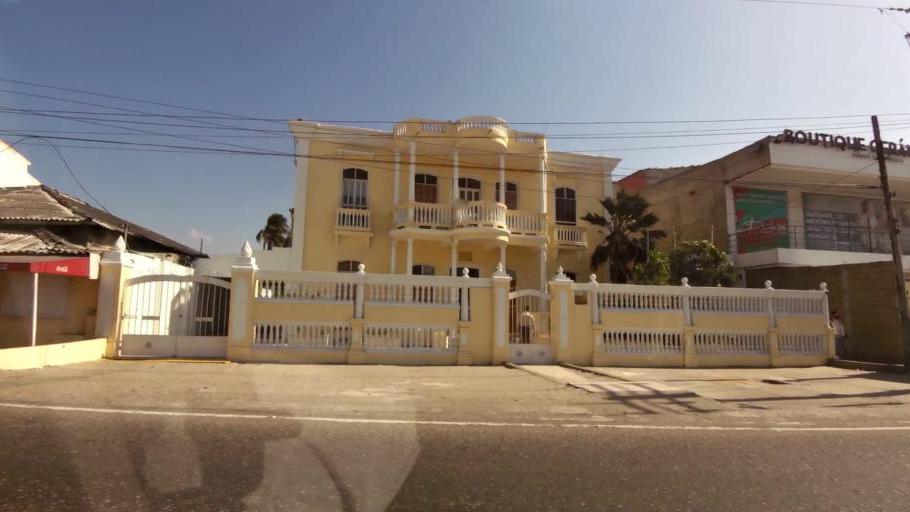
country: CO
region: Bolivar
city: Cartagena
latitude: 10.4318
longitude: -75.5447
